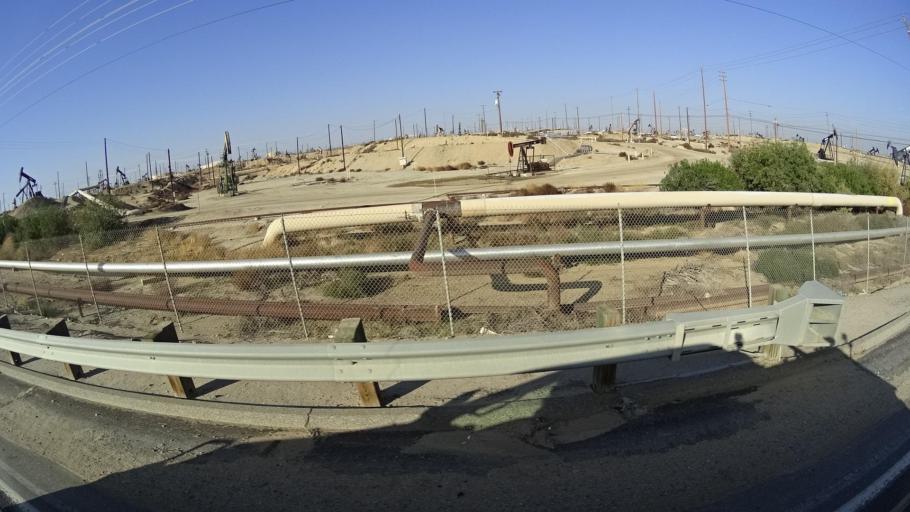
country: US
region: California
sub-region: Kern County
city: Oildale
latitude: 35.4269
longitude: -118.9826
